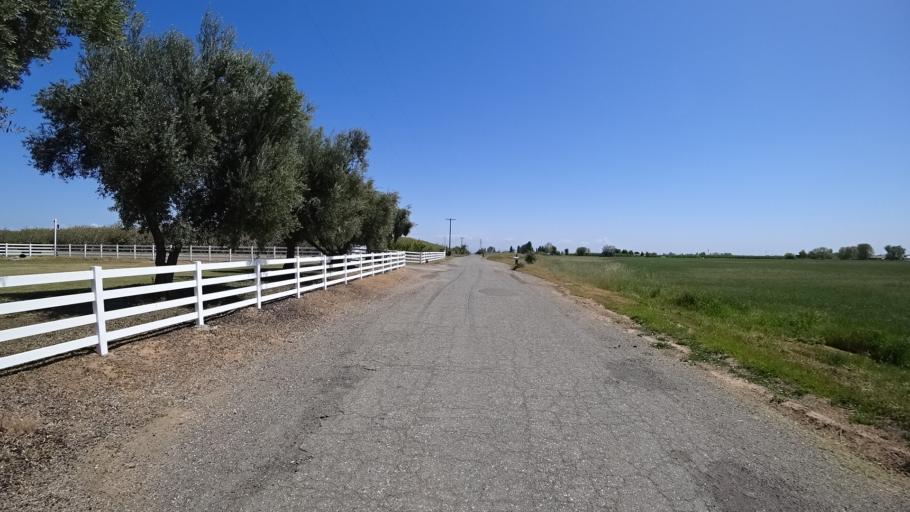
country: US
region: California
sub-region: Glenn County
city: Orland
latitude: 39.7797
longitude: -122.1553
